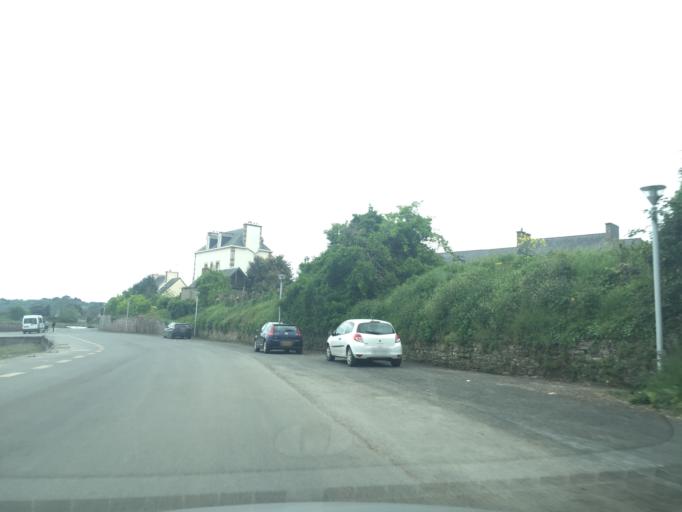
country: FR
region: Brittany
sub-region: Departement des Cotes-d'Armor
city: Paimpol
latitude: 48.7750
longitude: -3.0299
